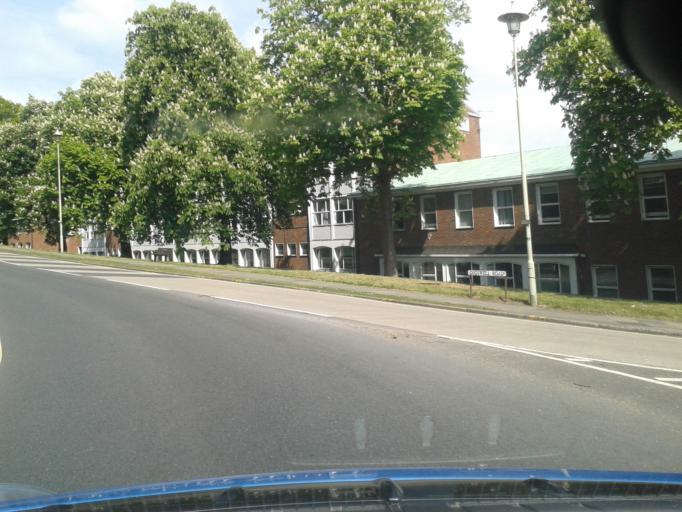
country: GB
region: England
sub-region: Hertfordshire
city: Welwyn Garden City
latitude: 51.8057
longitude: -0.2064
